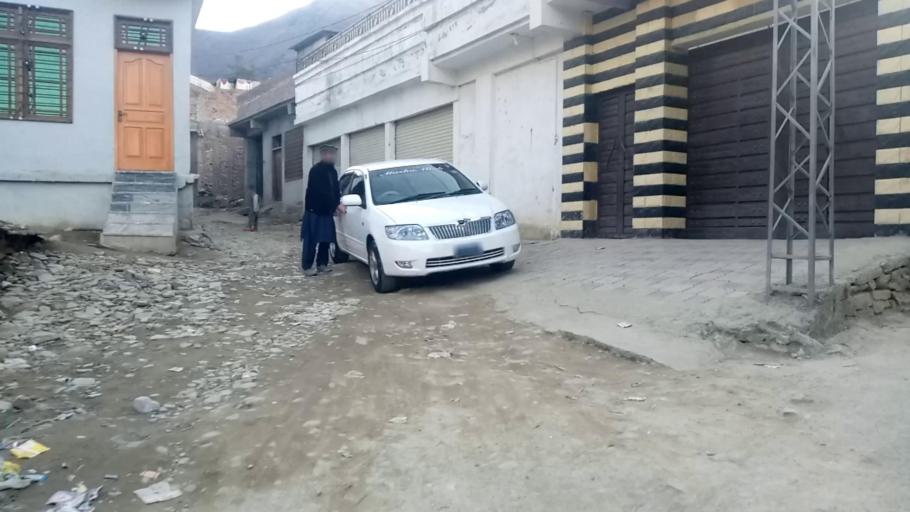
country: PK
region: Khyber Pakhtunkhwa
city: Saidu Sharif
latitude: 34.7385
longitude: 72.3520
